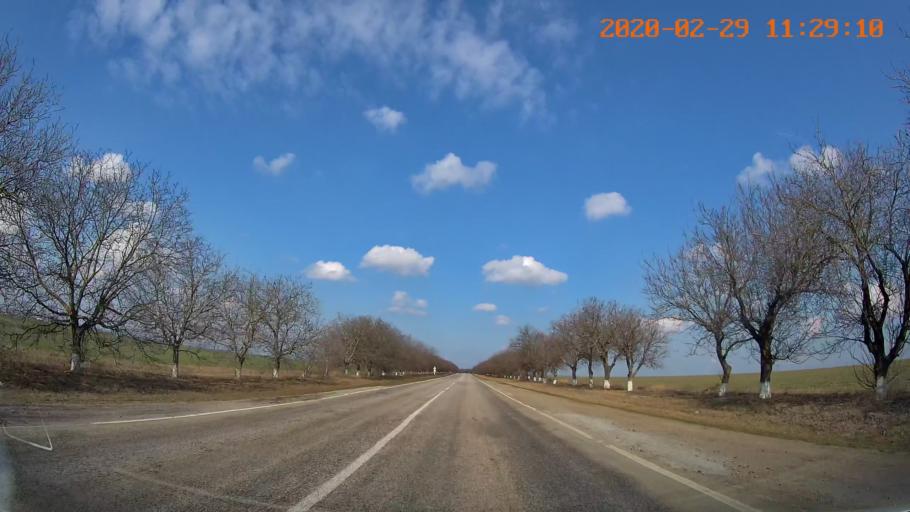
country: MD
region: Telenesti
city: Cocieri
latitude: 47.4903
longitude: 29.1278
